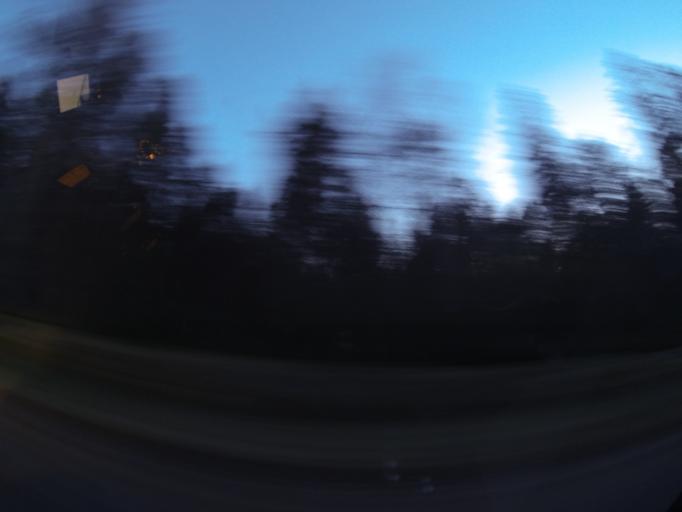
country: SE
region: OErebro
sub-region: Lindesbergs Kommun
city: Fellingsbro
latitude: 59.3748
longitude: 15.6203
